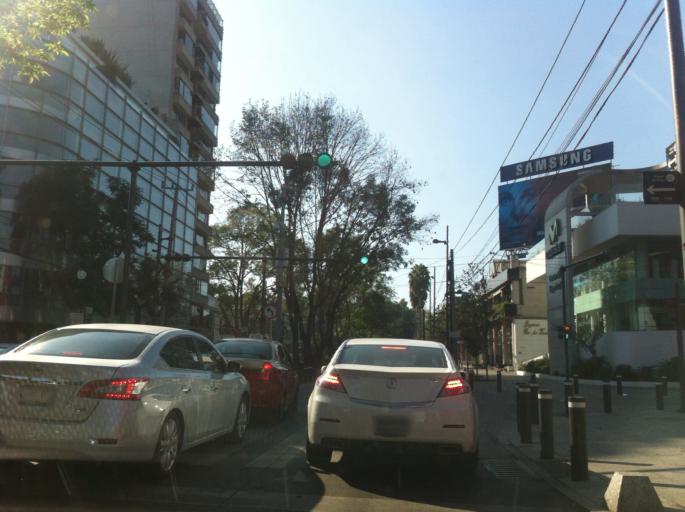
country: MX
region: Mexico City
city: Miguel Hidalgo
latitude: 19.4318
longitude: -99.1974
